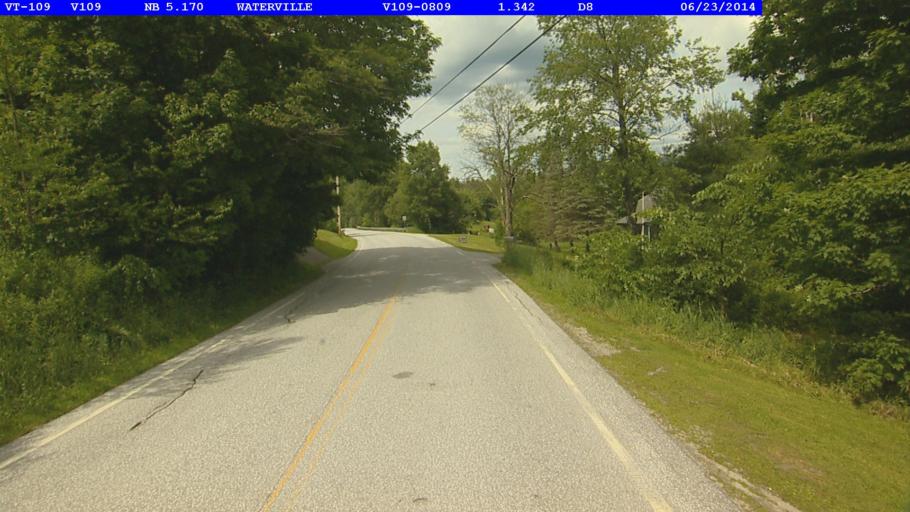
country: US
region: Vermont
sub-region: Lamoille County
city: Johnson
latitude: 44.7008
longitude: -72.7641
